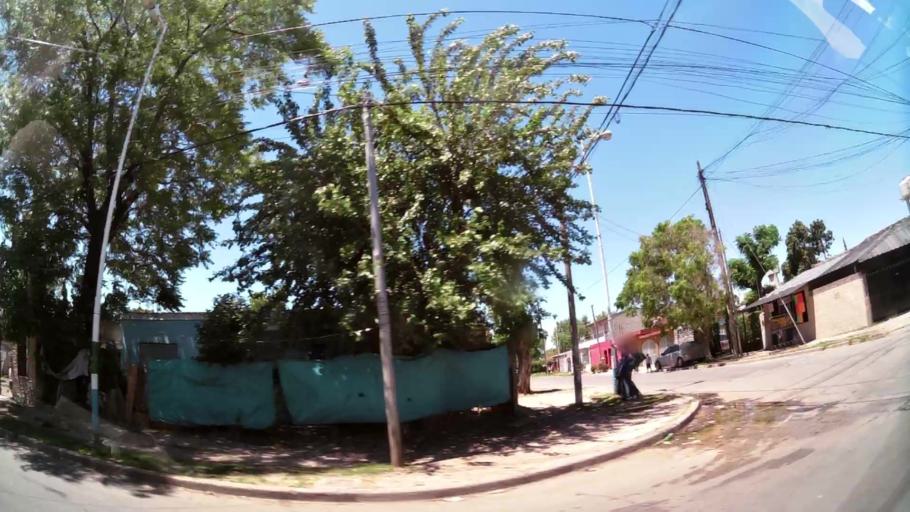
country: AR
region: Buenos Aires
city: Hurlingham
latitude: -34.5089
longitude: -58.7106
